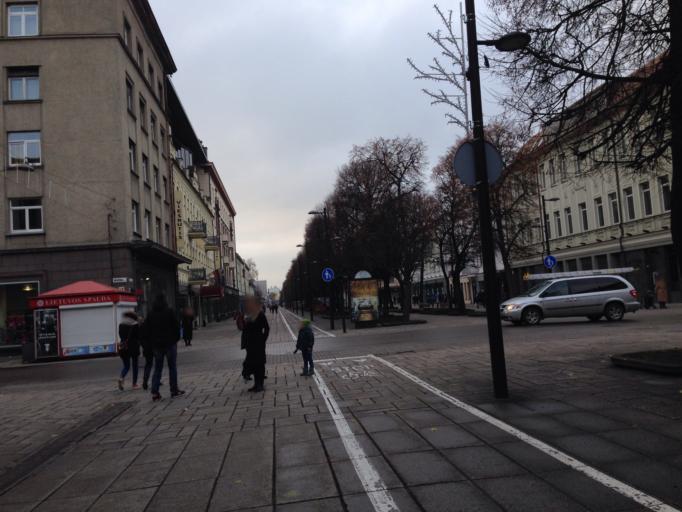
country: LT
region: Kauno apskritis
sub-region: Kaunas
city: Kaunas
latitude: 54.8975
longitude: 23.9100
